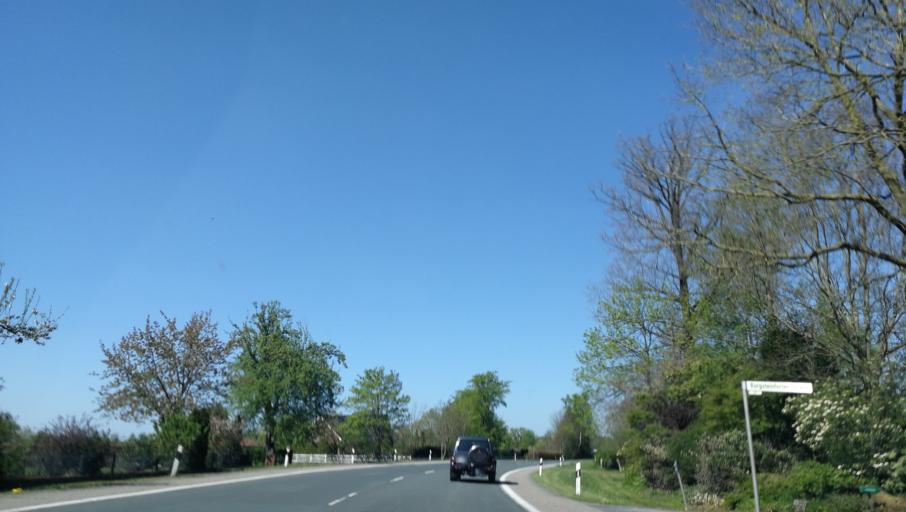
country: DE
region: North Rhine-Westphalia
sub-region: Regierungsbezirk Munster
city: Wettringen
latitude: 52.1944
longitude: 7.3244
